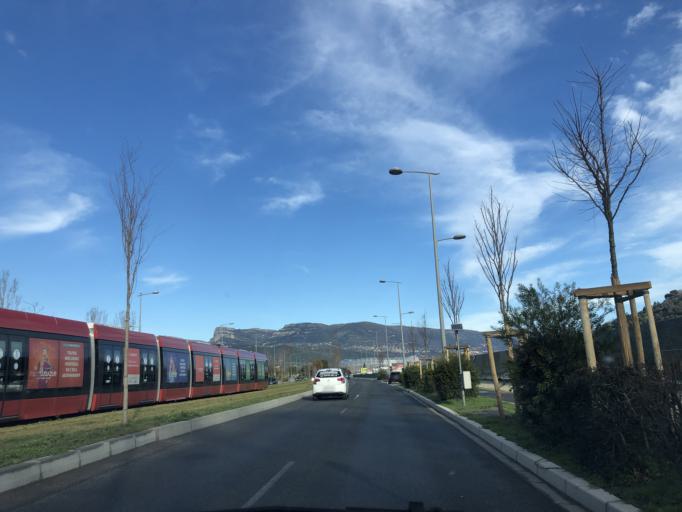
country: FR
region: Provence-Alpes-Cote d'Azur
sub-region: Departement des Alpes-Maritimes
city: Saint-Laurent-du-Var
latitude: 43.6931
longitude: 7.1992
